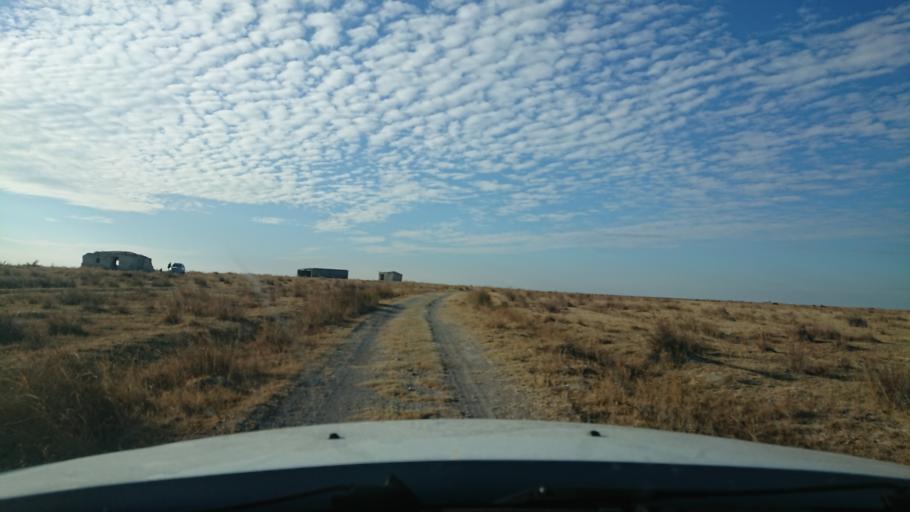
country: TR
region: Aksaray
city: Eskil
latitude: 38.5454
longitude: 33.3215
